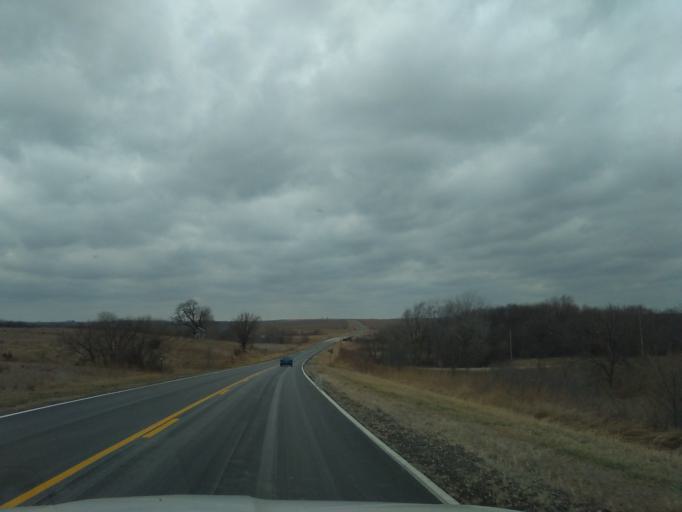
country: US
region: Nebraska
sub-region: Pawnee County
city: Pawnee City
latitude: 40.0510
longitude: -95.9977
